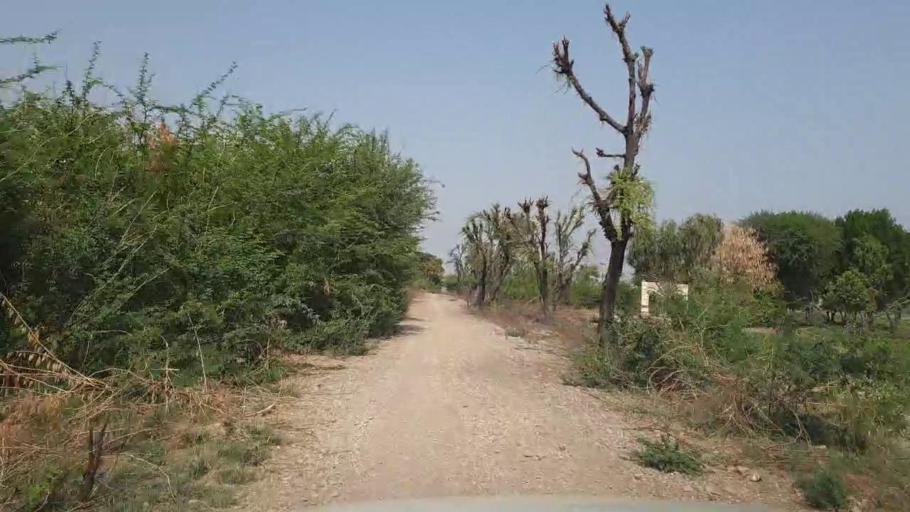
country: PK
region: Sindh
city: Dhoro Naro
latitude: 25.4882
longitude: 69.6582
